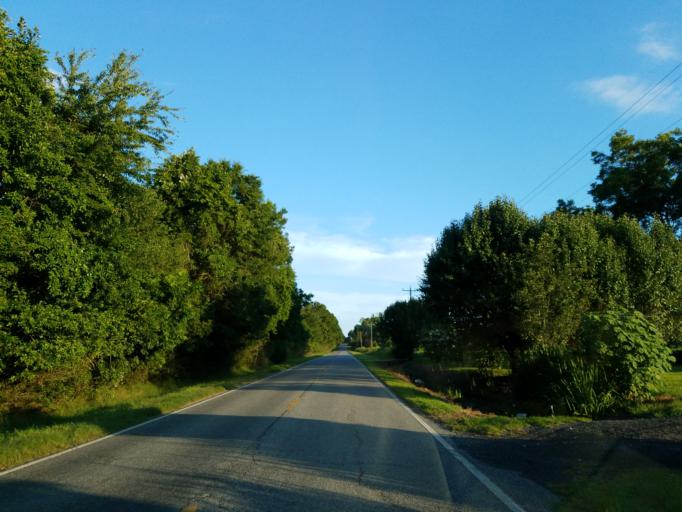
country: US
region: Georgia
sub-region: Cook County
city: Sparks
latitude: 31.2894
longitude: -83.4688
